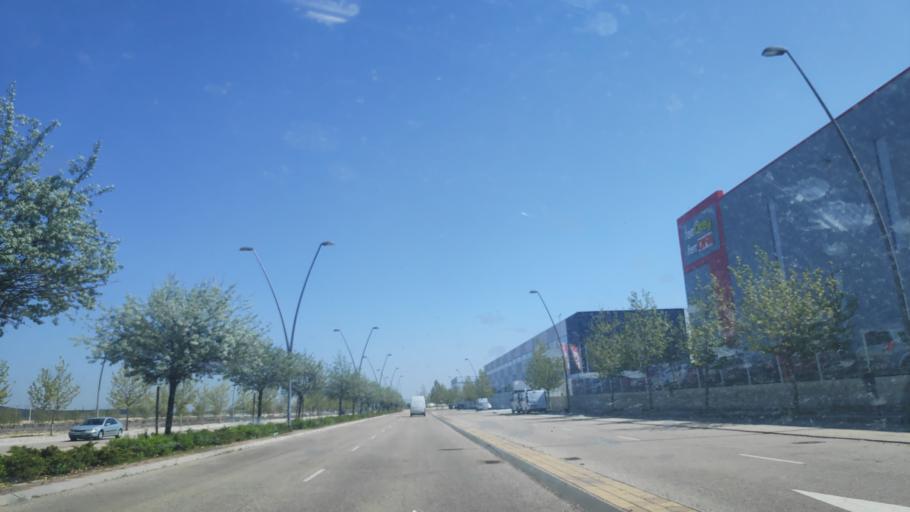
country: ES
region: Madrid
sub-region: Provincia de Madrid
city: Pinto
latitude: 40.2852
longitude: -3.6841
